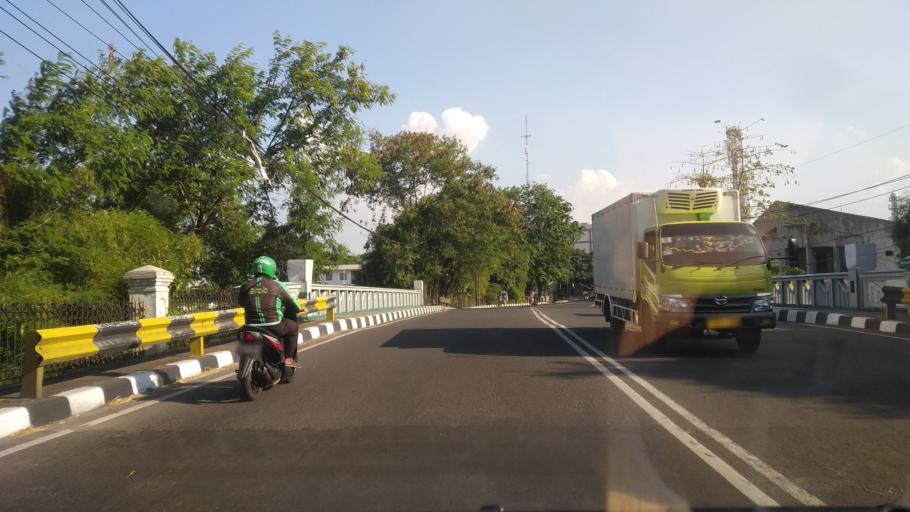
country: ID
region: Banten
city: South Tangerang
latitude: -6.2541
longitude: 106.7692
